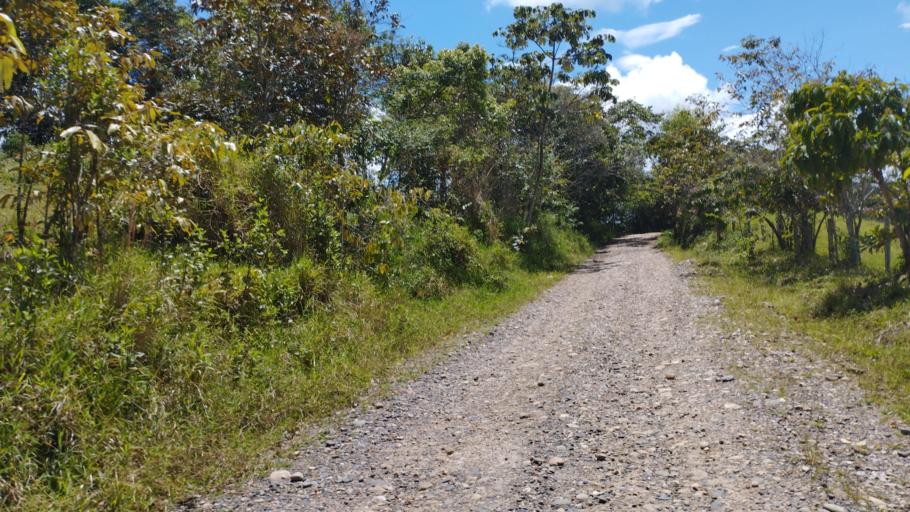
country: CO
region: Boyaca
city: San Luis de Gaceno
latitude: 4.7447
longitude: -73.1449
